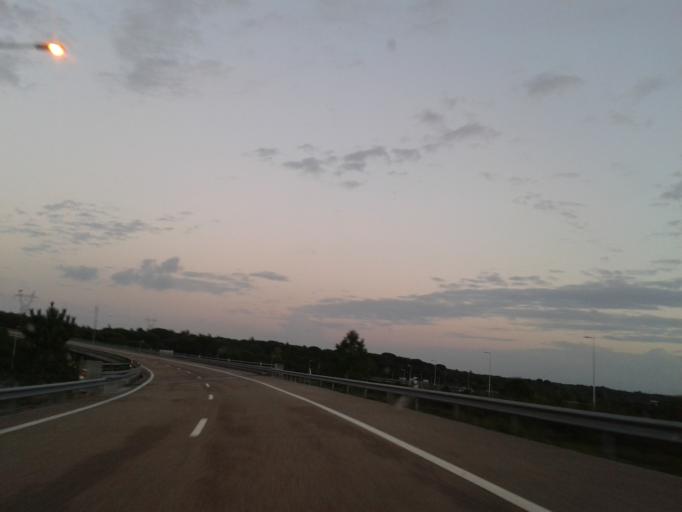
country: PT
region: Evora
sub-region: Vendas Novas
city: Vendas Novas
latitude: 38.6021
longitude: -8.6445
